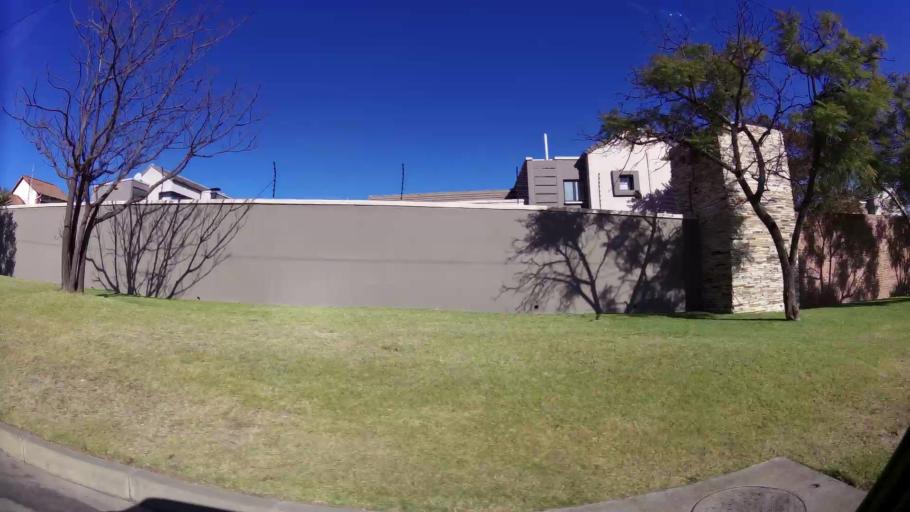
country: ZA
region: Gauteng
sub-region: West Rand District Municipality
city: Muldersdriseloop
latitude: -26.0525
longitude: 27.9616
